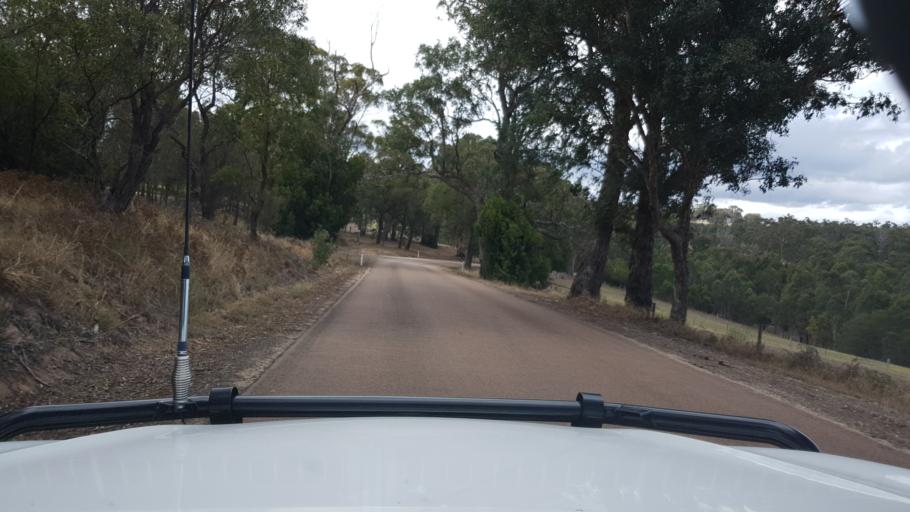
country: AU
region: Victoria
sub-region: East Gippsland
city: Bairnsdale
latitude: -37.7881
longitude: 147.5866
